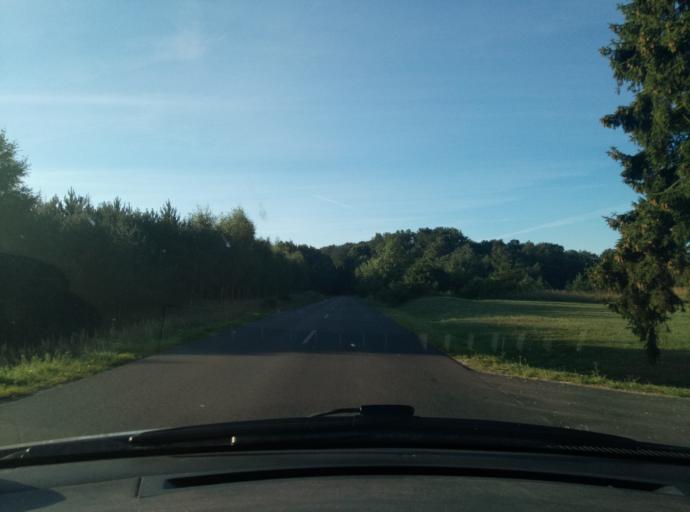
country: PL
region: Kujawsko-Pomorskie
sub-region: Powiat wabrzeski
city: Wabrzezno
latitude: 53.2380
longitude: 18.9436
